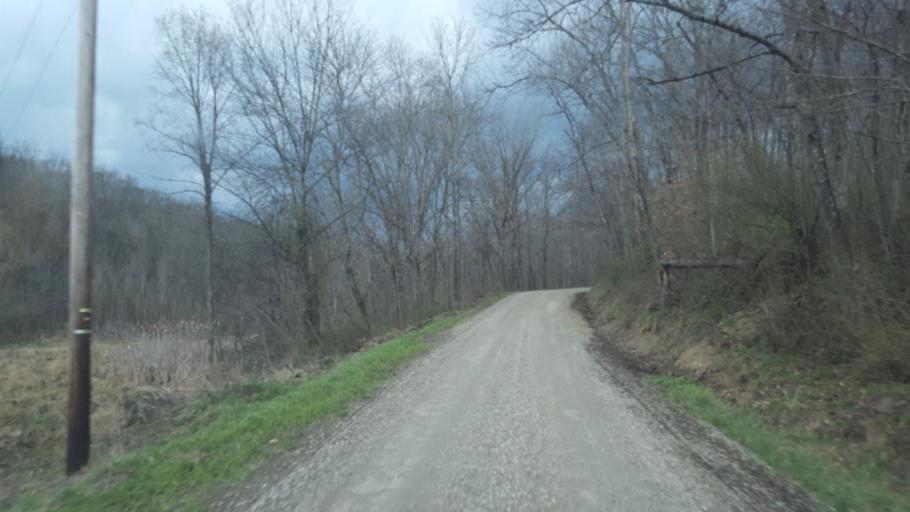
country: US
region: Ohio
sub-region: Guernsey County
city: Mantua
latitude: 40.1115
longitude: -81.8109
